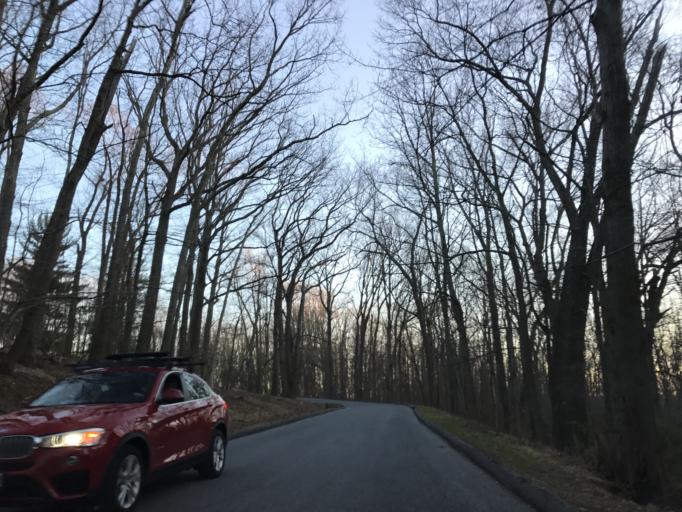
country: US
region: Maryland
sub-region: Carroll County
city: Eldersburg
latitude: 39.3596
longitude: -76.8900
